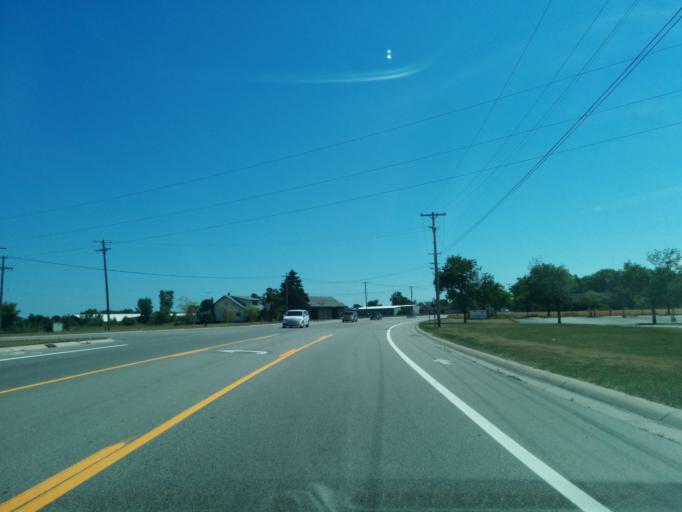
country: US
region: Michigan
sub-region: Bay County
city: Bay City
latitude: 43.5654
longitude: -83.9395
